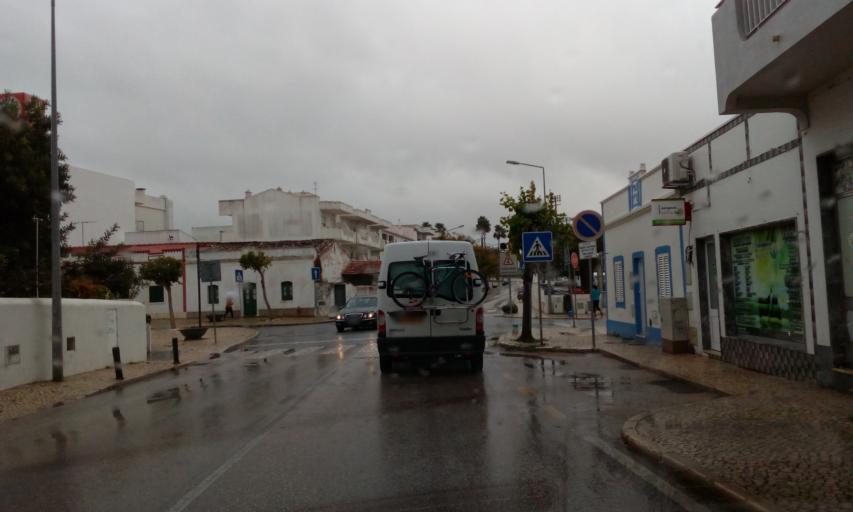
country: PT
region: Faro
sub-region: Albufeira
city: Guia
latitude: 37.1272
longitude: -8.3011
